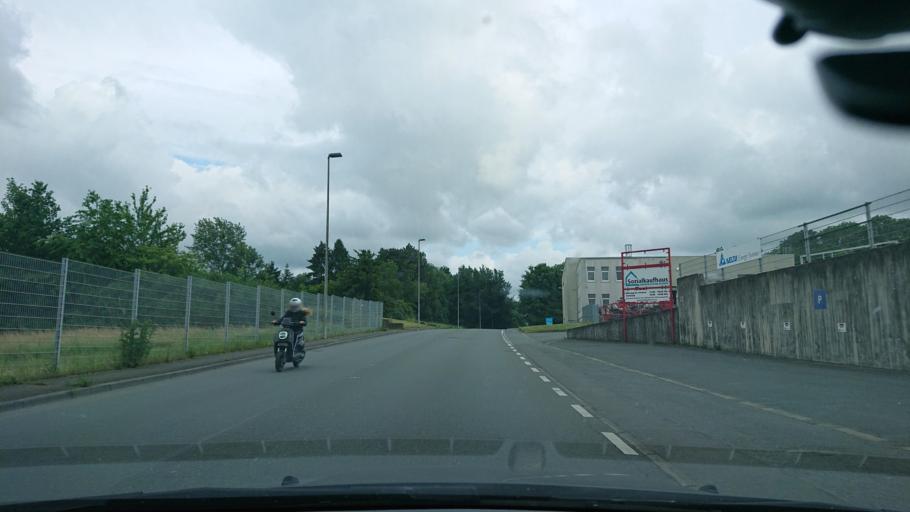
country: DE
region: North Rhine-Westphalia
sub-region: Regierungsbezirk Arnsberg
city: Soest
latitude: 51.5606
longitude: 8.1354
